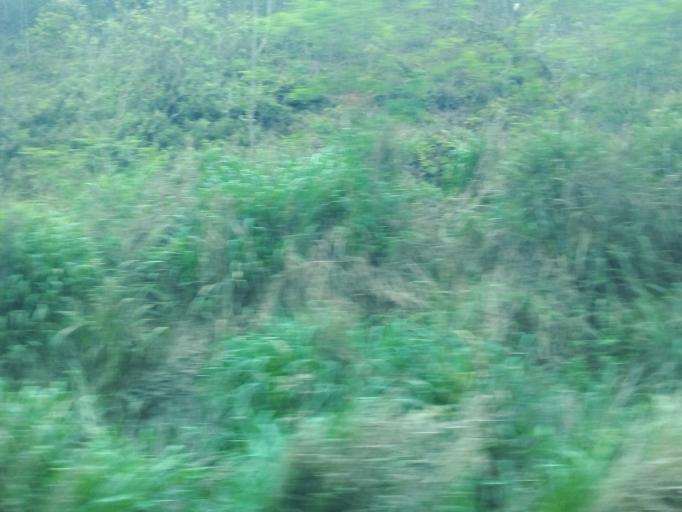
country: BR
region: Minas Gerais
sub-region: Ipaba
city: Ipaba
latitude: -19.4611
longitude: -42.4618
